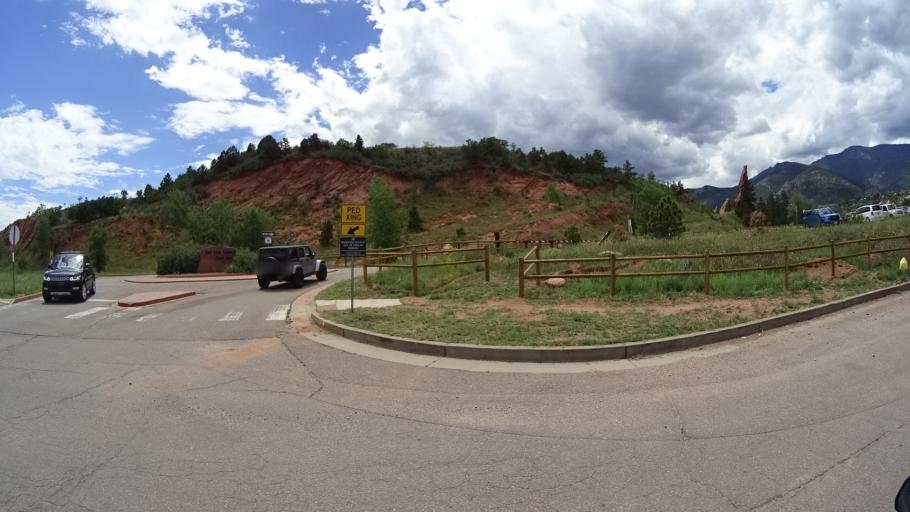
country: US
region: Colorado
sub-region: El Paso County
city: Manitou Springs
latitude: 38.8537
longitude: -104.8829
